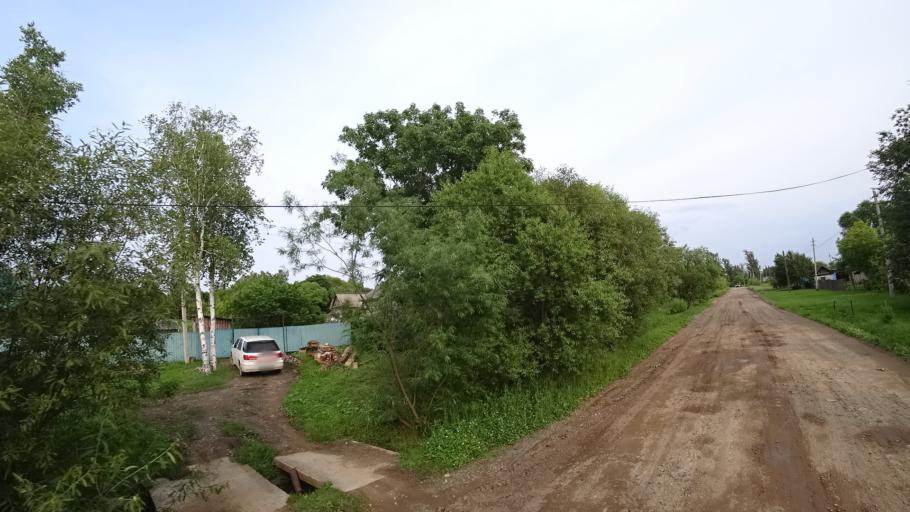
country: RU
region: Primorskiy
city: Novosysoyevka
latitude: 44.2498
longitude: 133.3767
